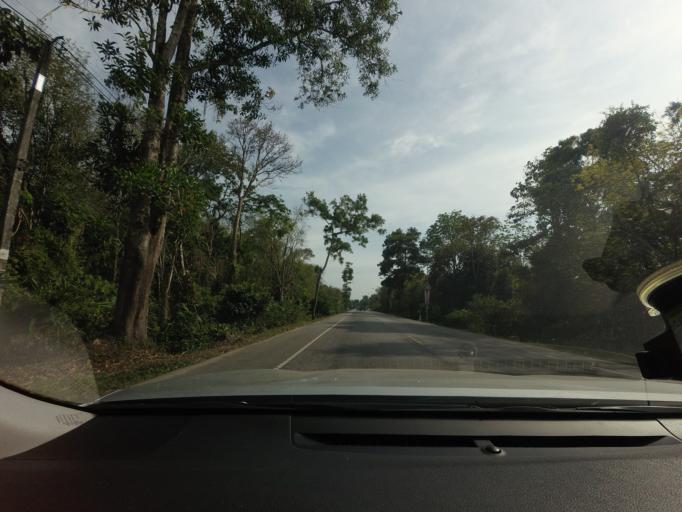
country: TH
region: Narathiwat
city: Ra-ngae
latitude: 6.3311
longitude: 101.7892
